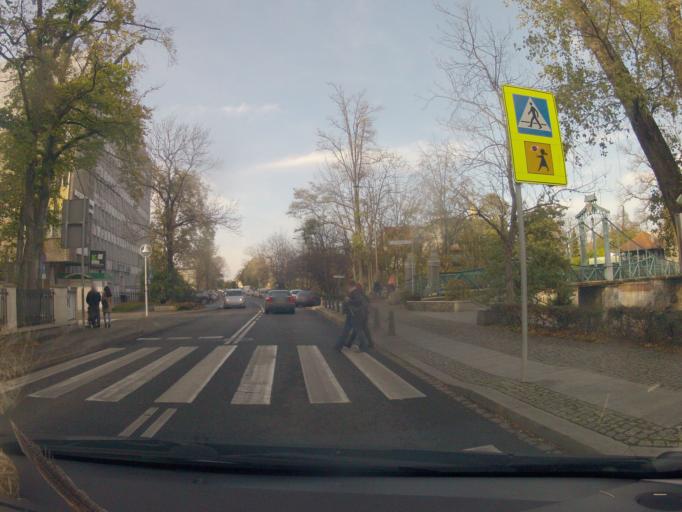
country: PL
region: Opole Voivodeship
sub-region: Powiat opolski
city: Opole
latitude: 50.6656
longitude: 17.9221
